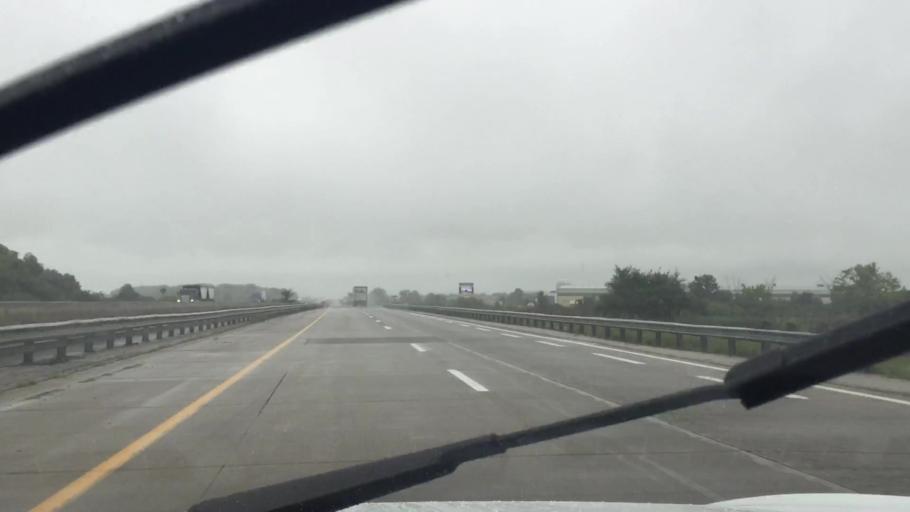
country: CA
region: Ontario
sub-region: Lambton County
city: Walpole Island
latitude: 42.2671
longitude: -82.4495
